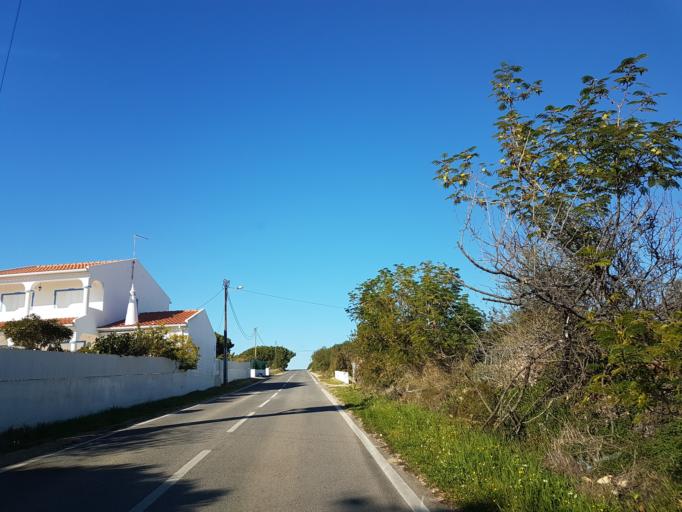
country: PT
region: Faro
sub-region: Lagoa
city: Carvoeiro
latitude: 37.0962
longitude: -8.4381
